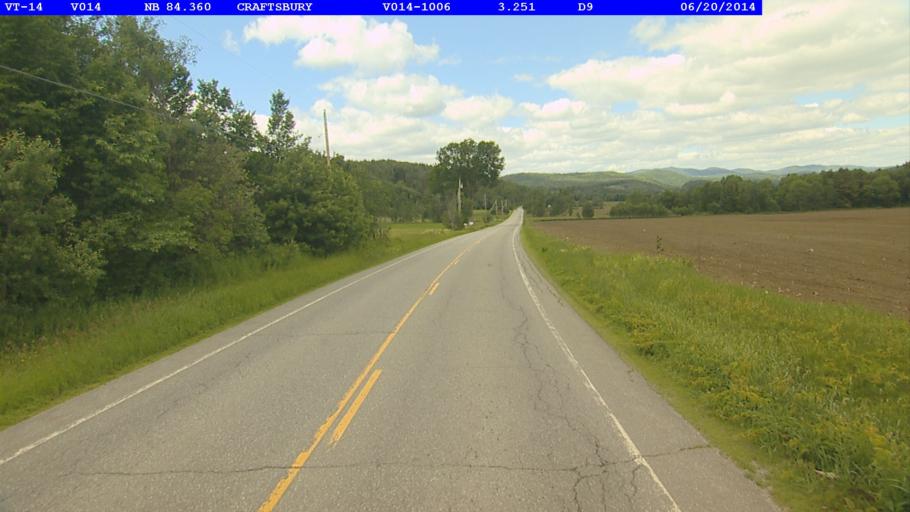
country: US
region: Vermont
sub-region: Caledonia County
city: Hardwick
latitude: 44.6383
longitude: -72.3992
